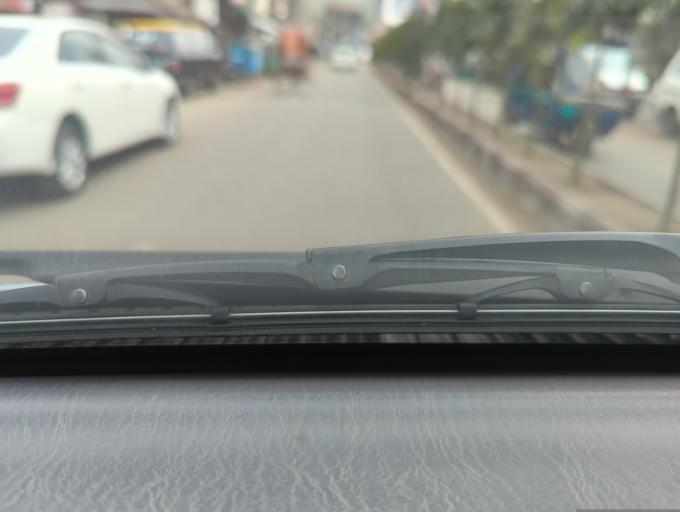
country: BD
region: Sylhet
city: Maulavi Bazar
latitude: 24.4884
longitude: 91.7634
